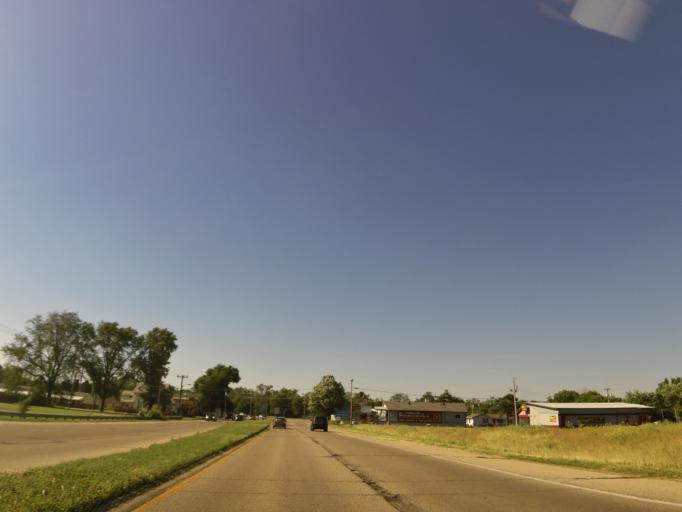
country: US
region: Illinois
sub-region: Winnebago County
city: South Beloit
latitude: 42.4951
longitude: -89.0198
